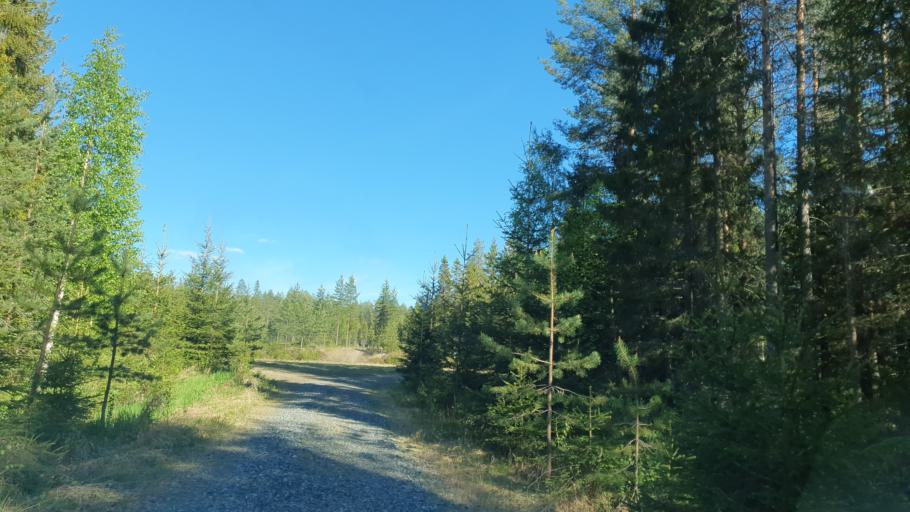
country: FI
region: Kainuu
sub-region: Kehys-Kainuu
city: Kuhmo
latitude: 64.1789
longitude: 29.4220
